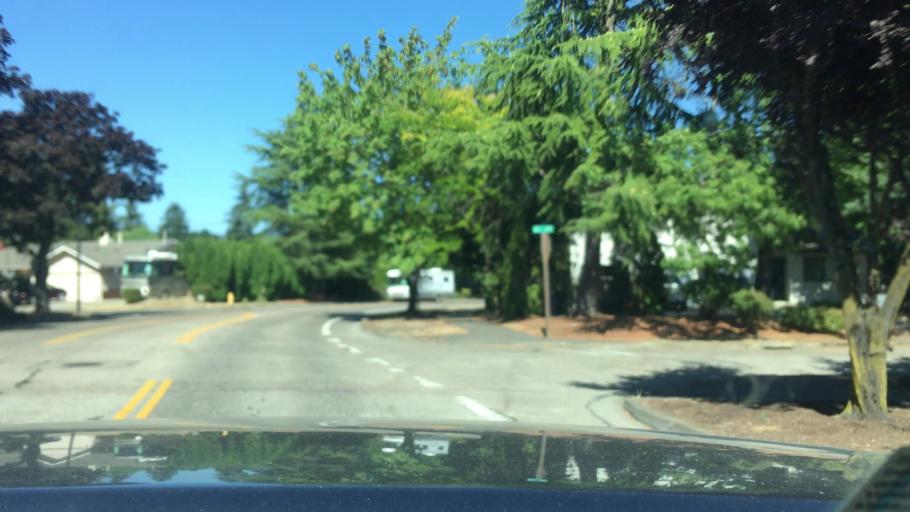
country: US
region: Oregon
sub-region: Lane County
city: Eugene
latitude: 44.0929
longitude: -123.0871
